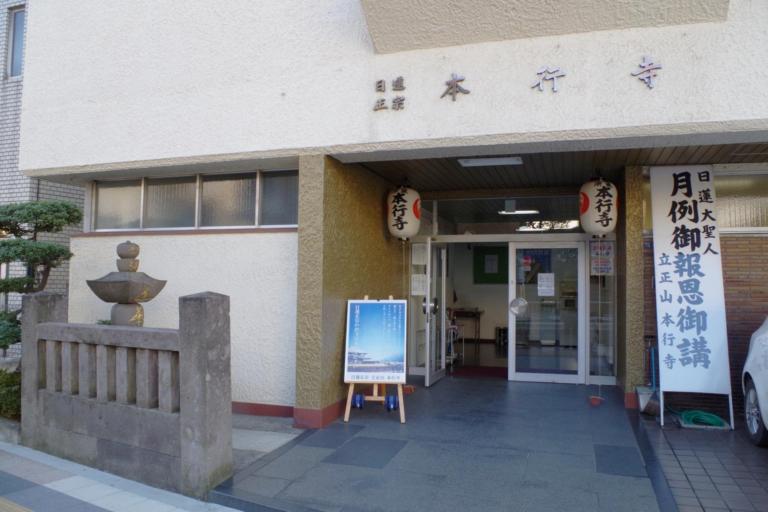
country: JP
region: Tokyo
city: Urayasu
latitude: 35.7122
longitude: 139.8068
